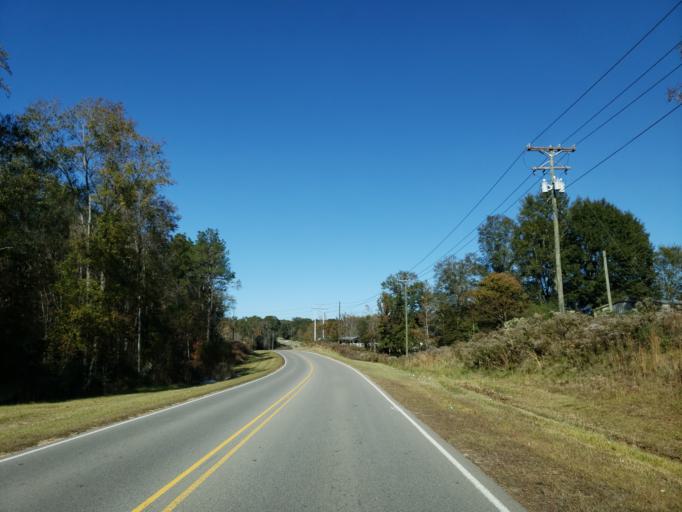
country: US
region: Mississippi
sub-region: Lamar County
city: Arnold Line
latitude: 31.3319
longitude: -89.3991
